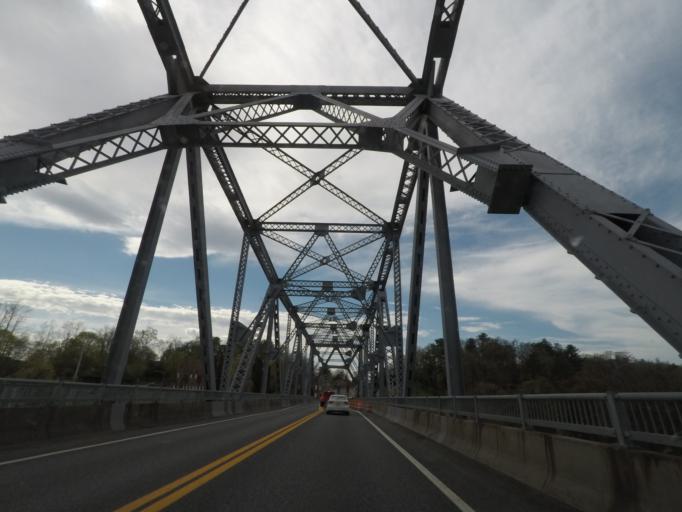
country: US
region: New York
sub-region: Greene County
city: Catskill
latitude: 42.2243
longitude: -73.8538
